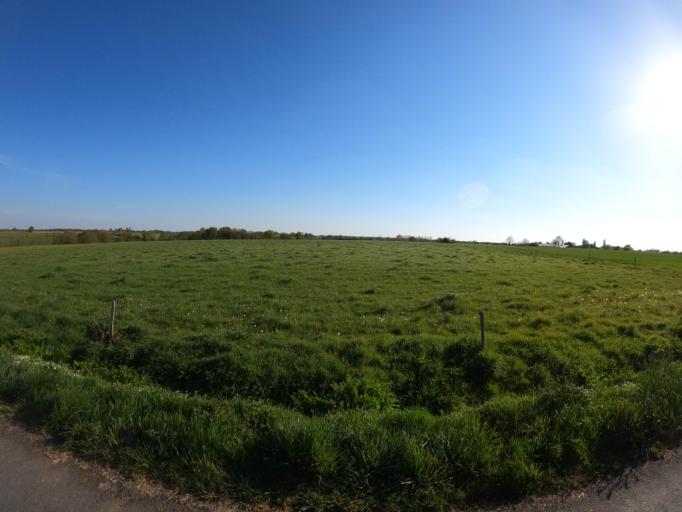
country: FR
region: Pays de la Loire
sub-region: Departement de la Vendee
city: Les Brouzils
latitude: 46.8882
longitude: -1.3421
